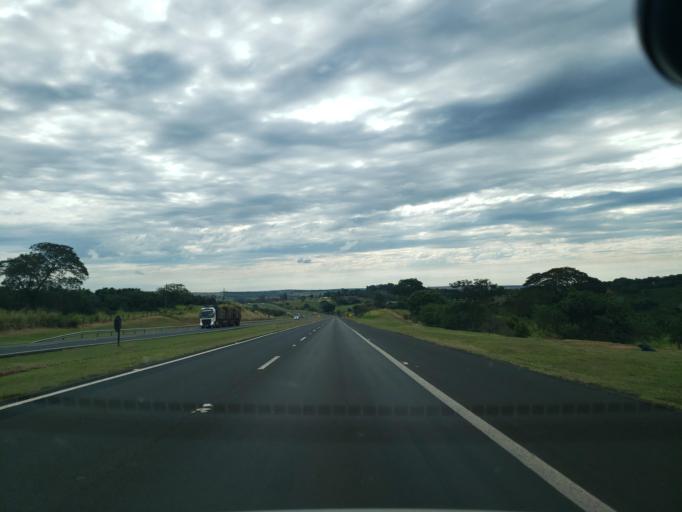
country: BR
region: Sao Paulo
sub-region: Bauru
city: Bauru
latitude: -22.2230
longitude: -49.1639
